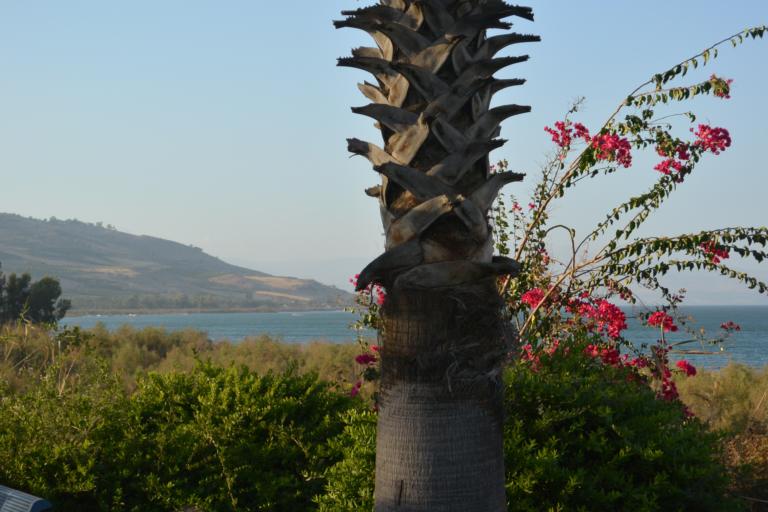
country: IL
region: Northern District
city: Yavne'el
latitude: 32.7074
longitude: 35.5805
